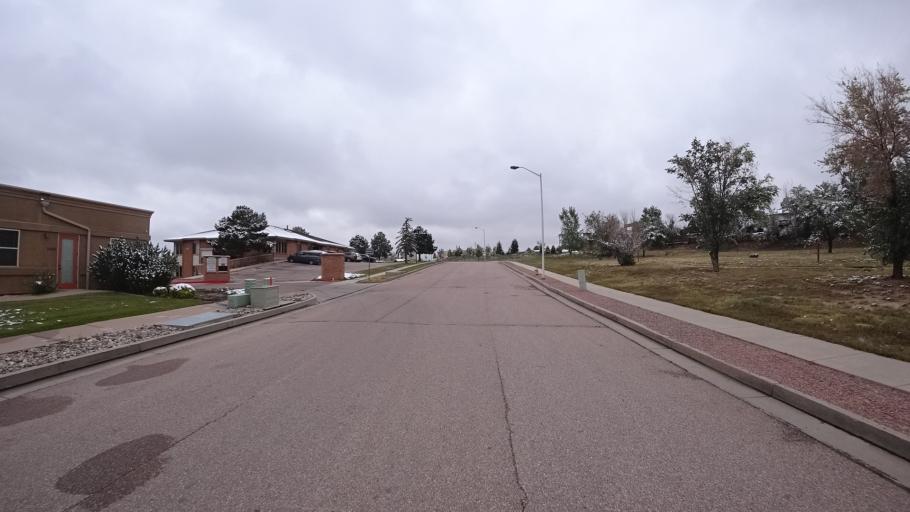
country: US
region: Colorado
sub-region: El Paso County
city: Colorado Springs
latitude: 38.9229
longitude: -104.7904
